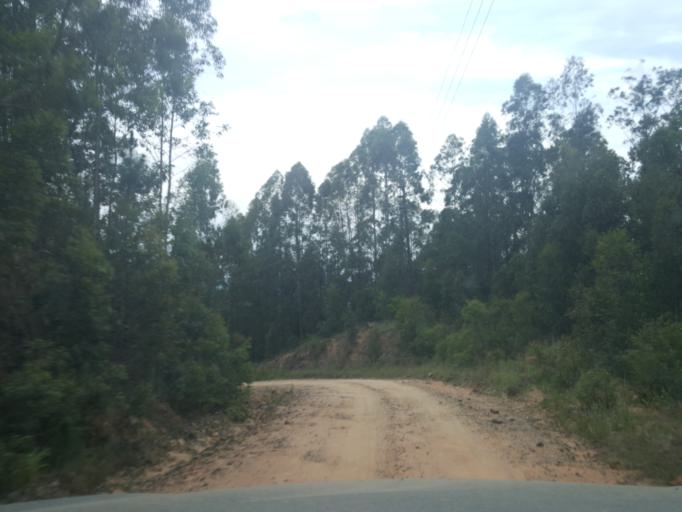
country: ZA
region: Limpopo
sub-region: Mopani District Municipality
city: Hoedspruit
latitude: -24.5963
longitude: 30.8721
